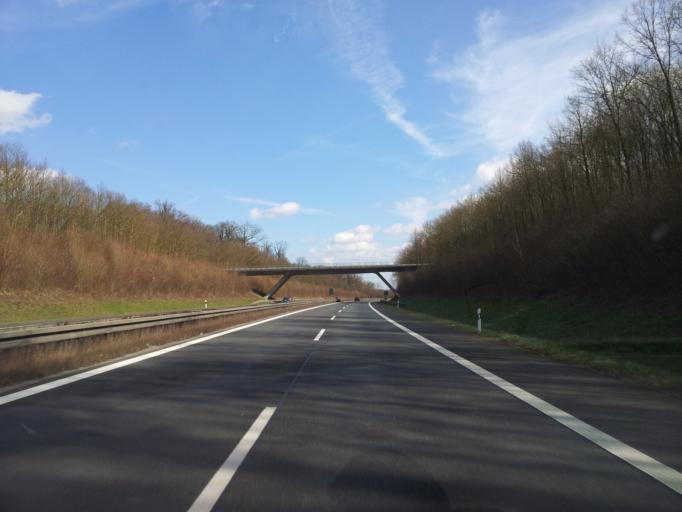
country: DE
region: Bavaria
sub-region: Regierungsbezirk Unterfranken
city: Hassfurt
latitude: 50.0041
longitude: 10.5052
